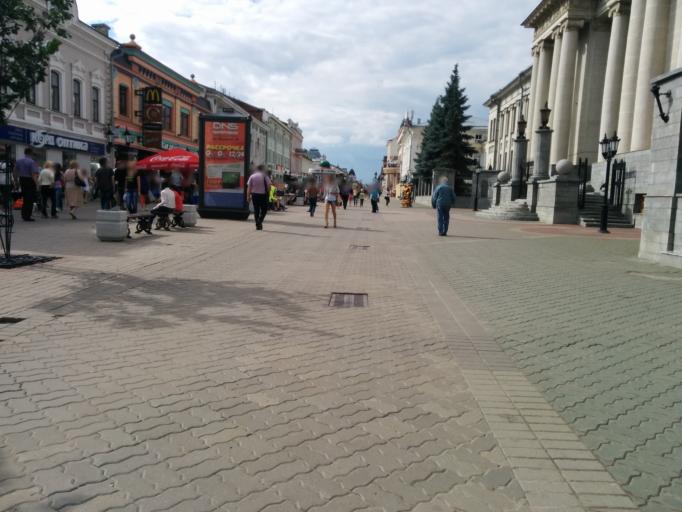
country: RU
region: Tatarstan
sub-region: Gorod Kazan'
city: Kazan
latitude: 55.7888
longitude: 49.1188
